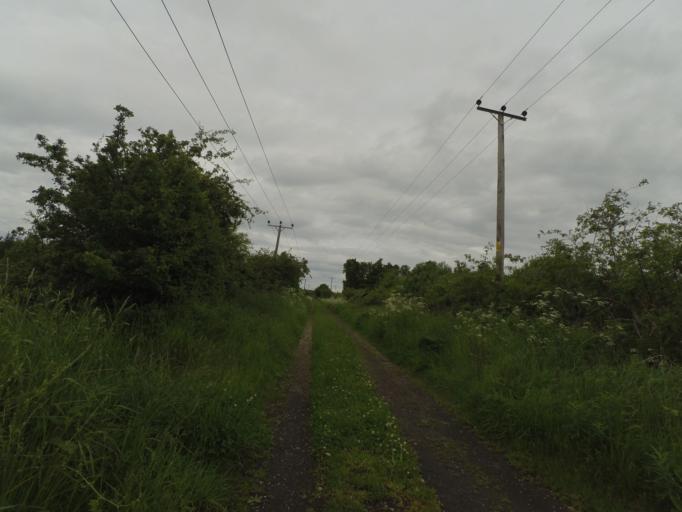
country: GB
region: Scotland
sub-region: East Lothian
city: Macmerry
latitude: 55.9268
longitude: -2.9096
